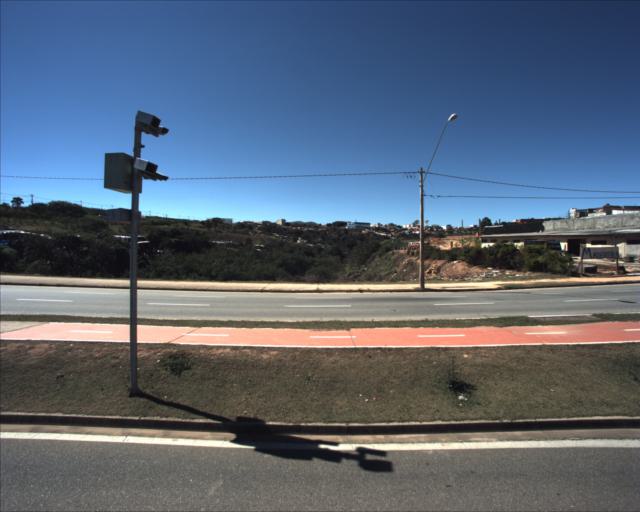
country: BR
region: Sao Paulo
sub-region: Sorocaba
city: Sorocaba
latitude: -23.4883
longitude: -47.4898
